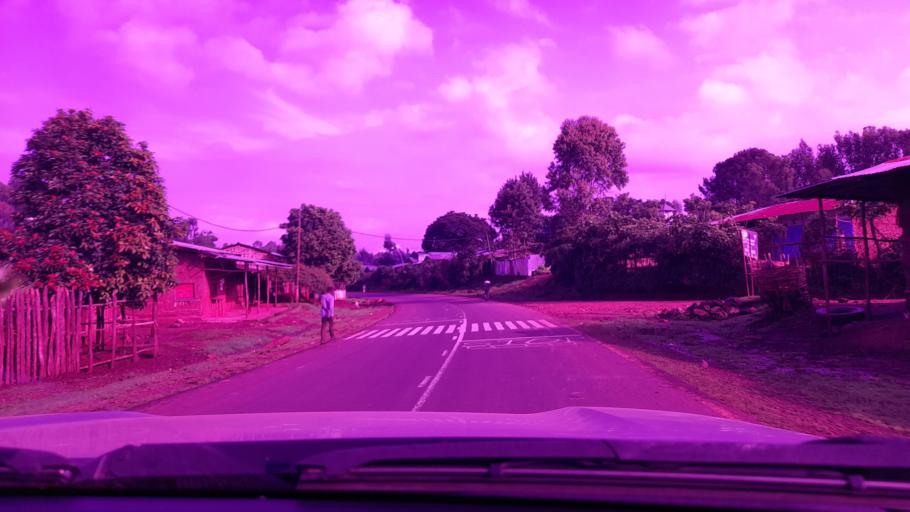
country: ET
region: Oromiya
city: Bedele
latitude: 8.1670
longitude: 36.4707
